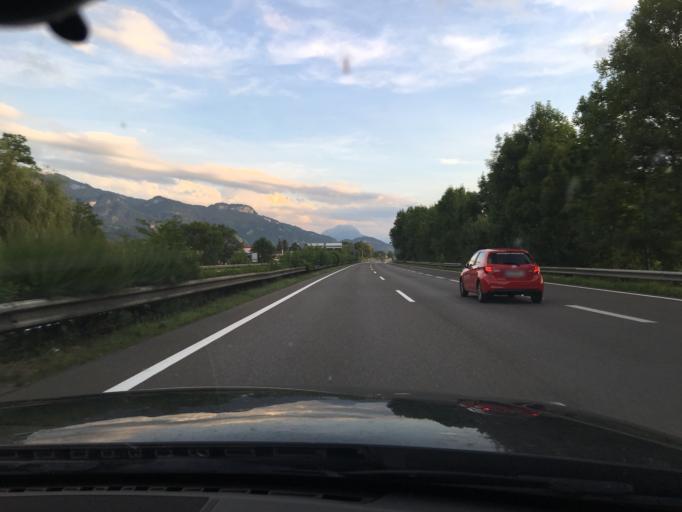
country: AT
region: Vorarlberg
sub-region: Politischer Bezirk Dornbirn
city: Dornbirn
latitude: 47.4117
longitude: 9.7069
